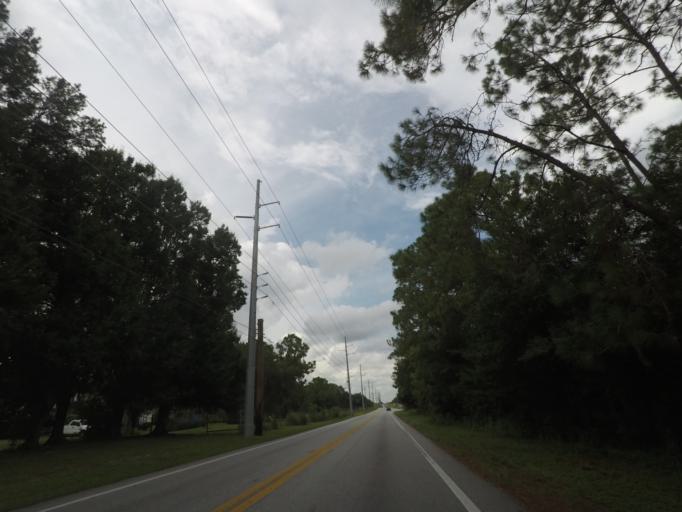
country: US
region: Florida
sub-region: Polk County
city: Loughman
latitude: 28.2482
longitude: -81.5905
